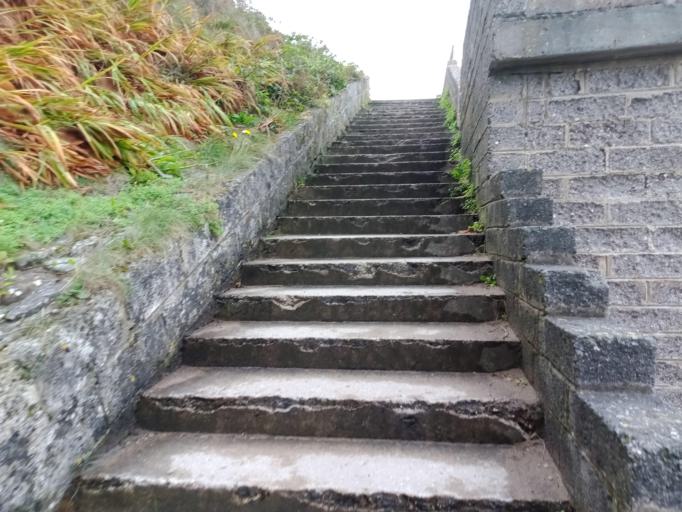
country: IE
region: Munster
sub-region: Waterford
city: Dungarvan
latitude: 52.0544
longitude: -7.5404
